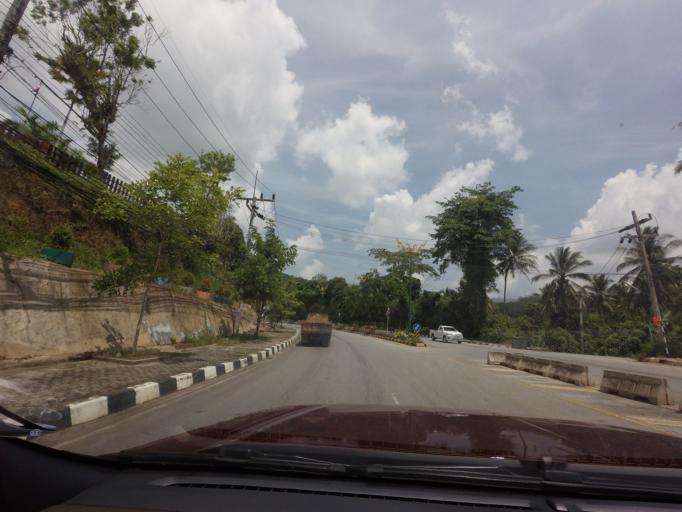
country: TH
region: Yala
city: Betong
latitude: 5.7740
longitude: 101.0604
